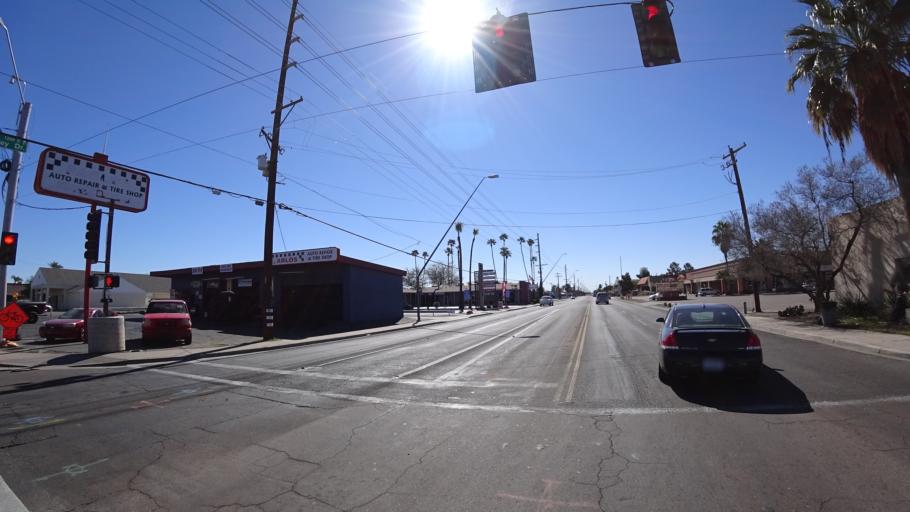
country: US
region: Arizona
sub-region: Maricopa County
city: Mesa
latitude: 33.4151
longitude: -111.8053
